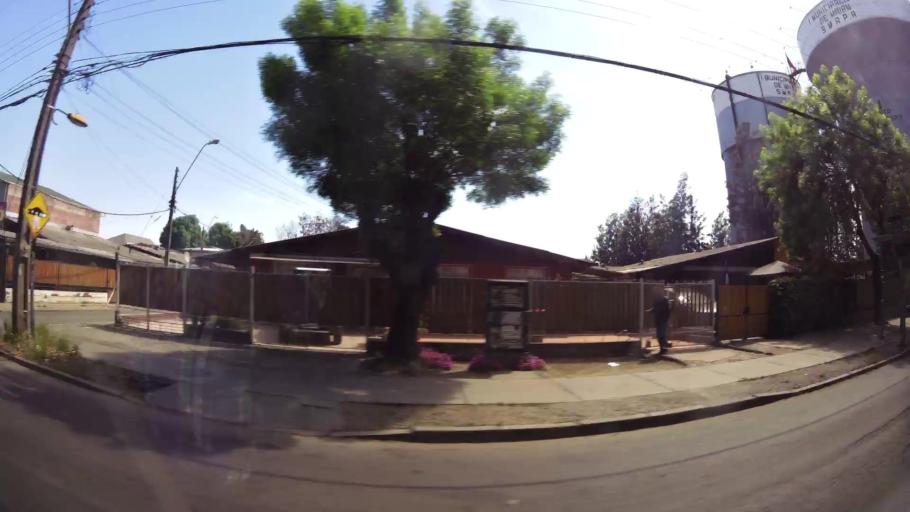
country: CL
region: Santiago Metropolitan
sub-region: Provincia de Santiago
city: Lo Prado
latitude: -33.4764
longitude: -70.7266
